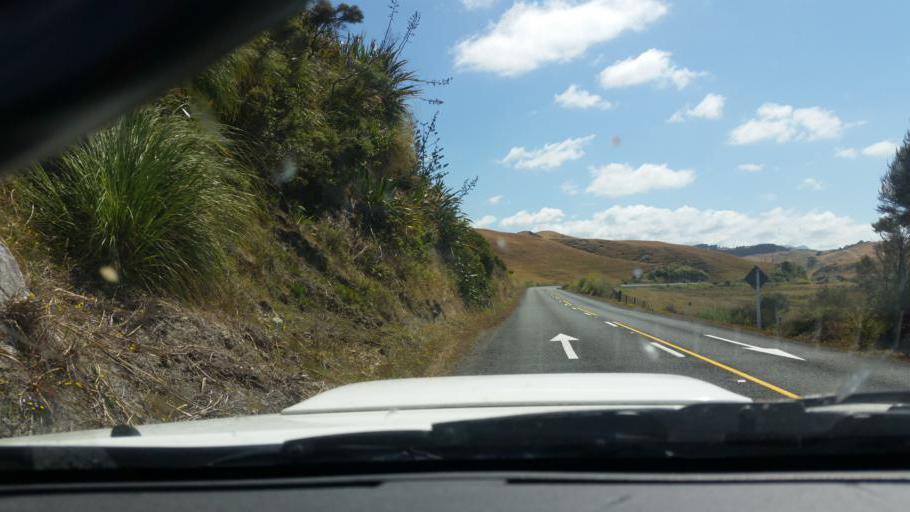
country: NZ
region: Northland
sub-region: Kaipara District
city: Dargaville
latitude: -35.8338
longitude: 173.6618
